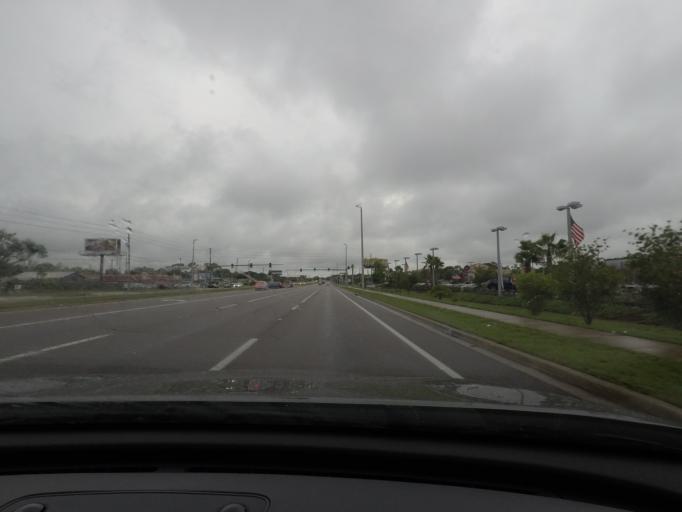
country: US
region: Florida
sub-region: Orange County
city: Union Park
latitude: 28.5685
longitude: -81.2766
